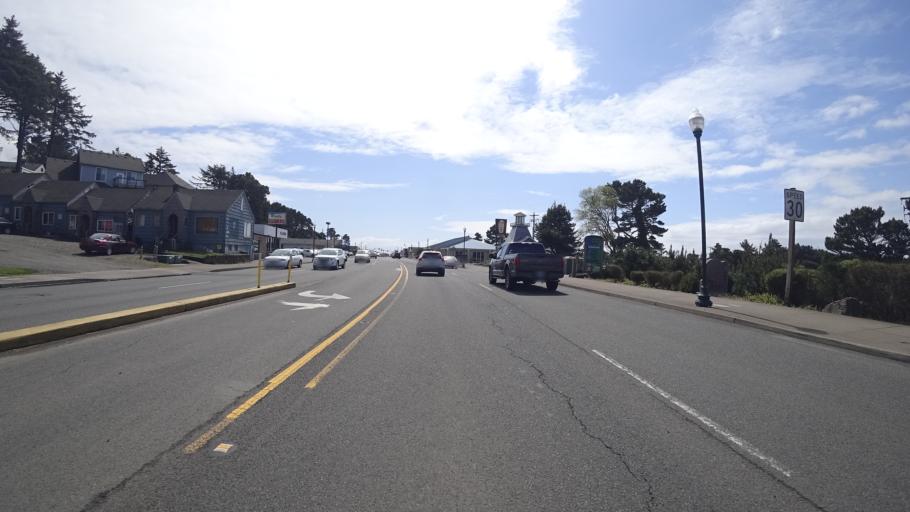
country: US
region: Oregon
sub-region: Lincoln County
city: Lincoln City
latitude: 44.9796
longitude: -124.0102
